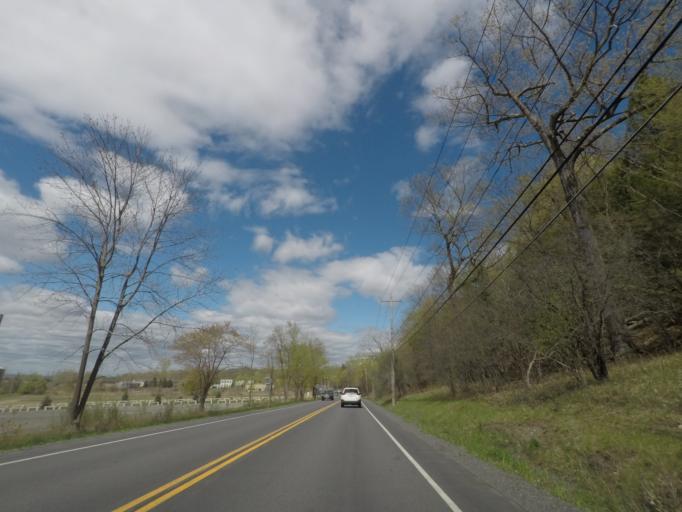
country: US
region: New York
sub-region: Columbia County
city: Oakdale
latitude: 42.2282
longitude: -73.7849
